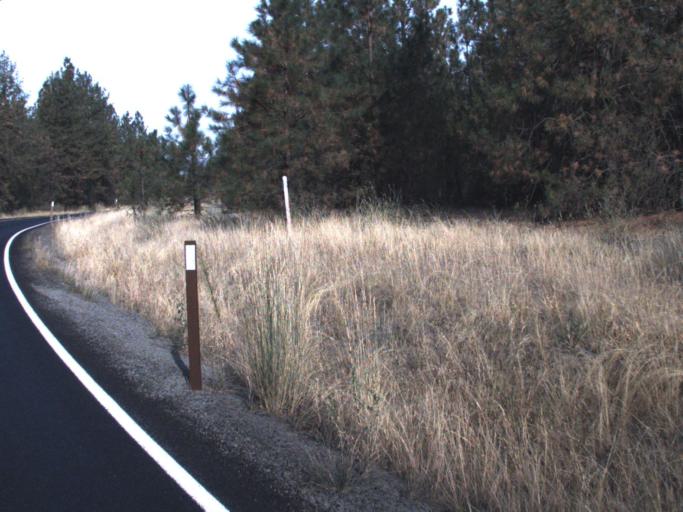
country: US
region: Washington
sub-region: Spokane County
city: Deer Park
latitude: 47.8405
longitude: -117.6141
